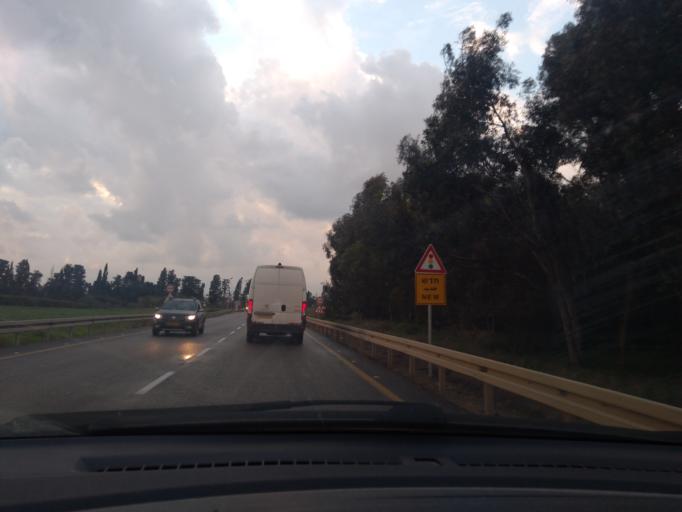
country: IL
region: Central District
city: Elyakhin
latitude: 32.3764
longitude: 34.8984
